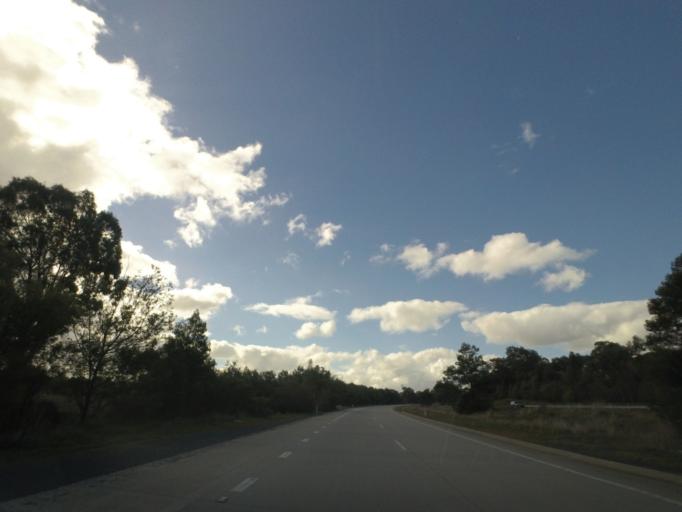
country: AU
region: New South Wales
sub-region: Greater Hume Shire
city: Holbrook
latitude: -35.8764
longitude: 147.1803
